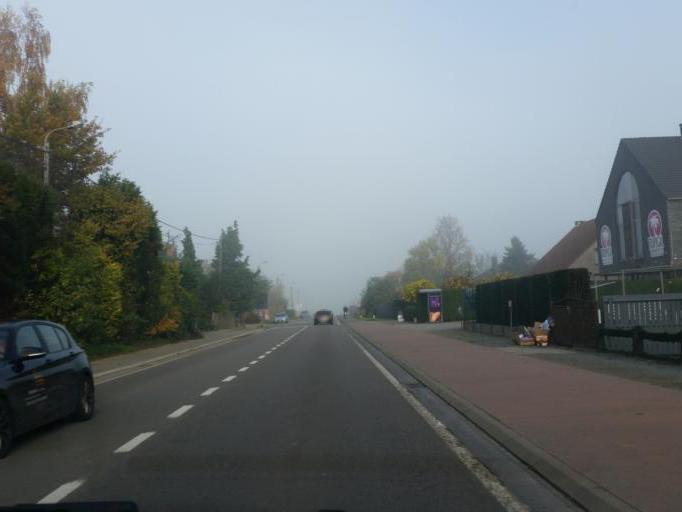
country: BE
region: Flanders
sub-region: Provincie Vlaams-Brabant
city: Opwijk
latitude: 50.9628
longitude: 4.1549
